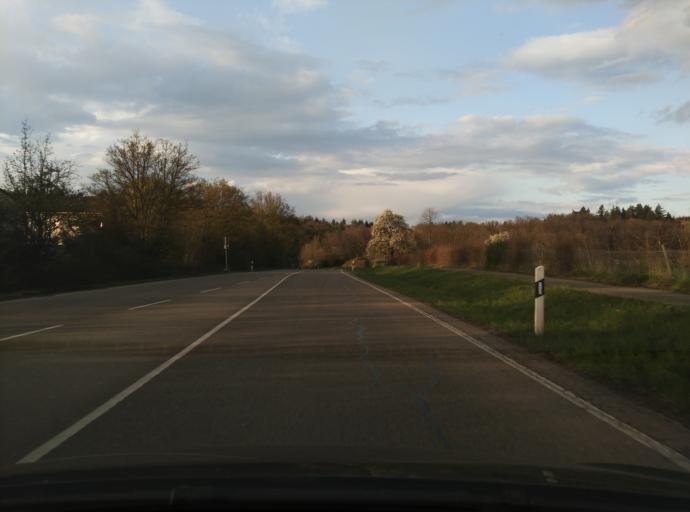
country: DE
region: Baden-Wuerttemberg
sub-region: Tuebingen Region
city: Metzingen
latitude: 48.5542
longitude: 9.2968
